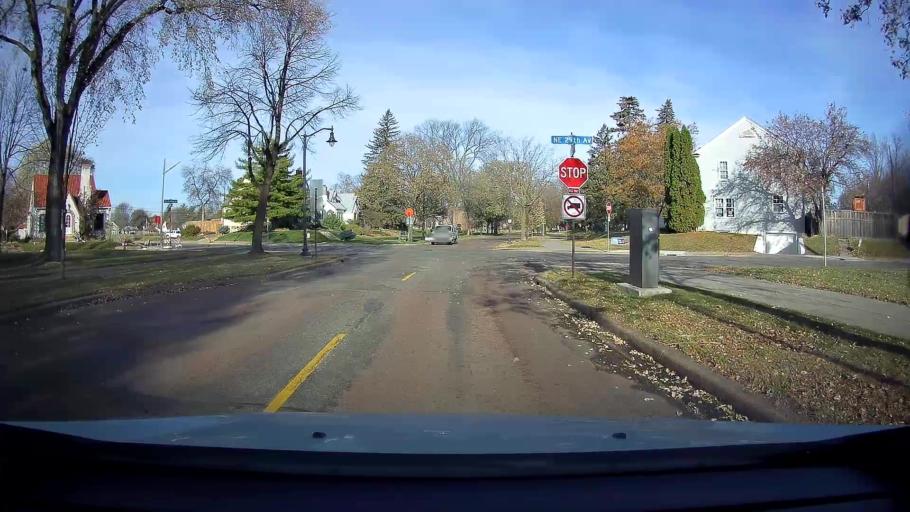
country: US
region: Minnesota
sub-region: Hennepin County
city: Saint Anthony
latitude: 45.0203
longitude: -93.2314
